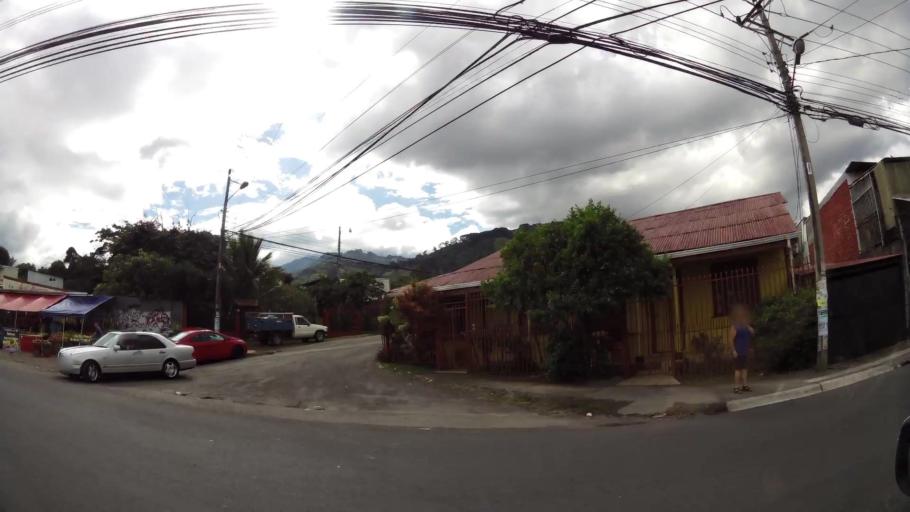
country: CR
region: San Jose
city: San Juan de Dios
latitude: 9.8810
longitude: -84.0840
